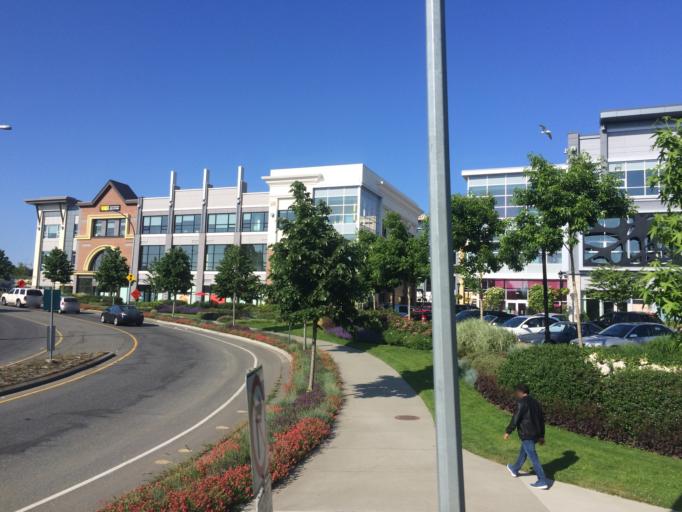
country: CA
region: British Columbia
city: Victoria
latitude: 48.4550
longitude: -123.3771
